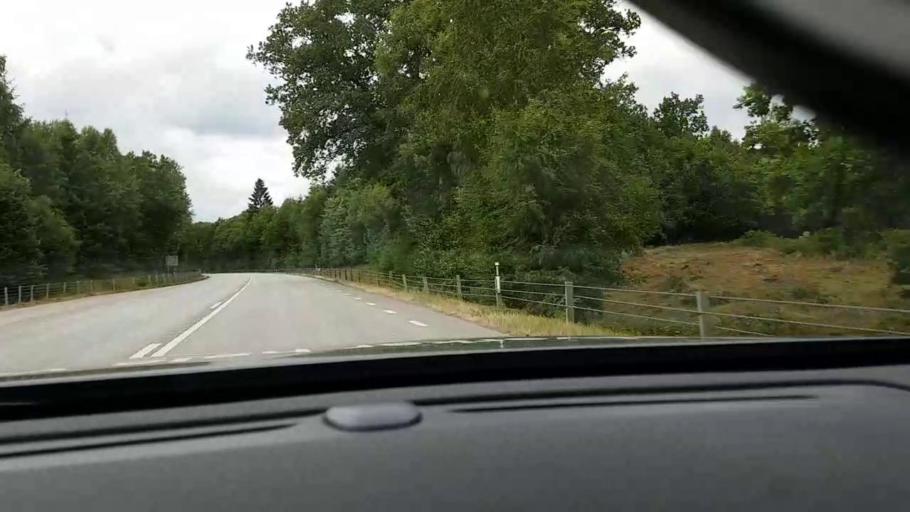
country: SE
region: Skane
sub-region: Horby Kommun
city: Hoerby
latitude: 55.8659
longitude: 13.6384
